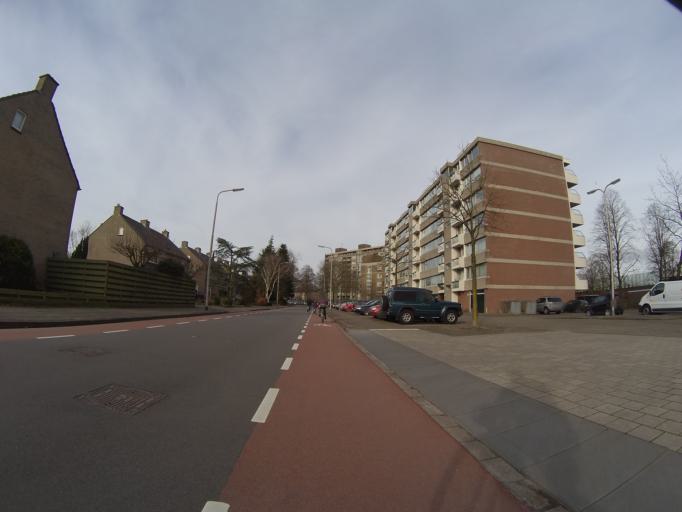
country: NL
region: Utrecht
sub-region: Gemeente Amersfoort
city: Randenbroek
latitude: 52.1521
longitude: 5.4138
